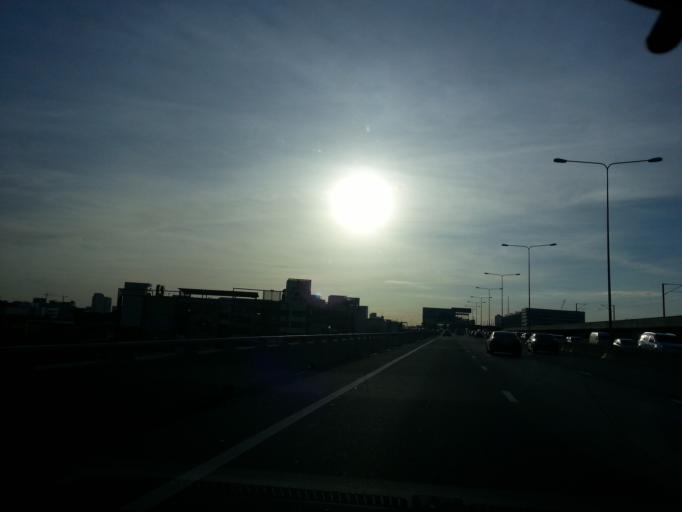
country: TH
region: Bangkok
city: Suan Luang
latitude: 13.7410
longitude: 100.6211
